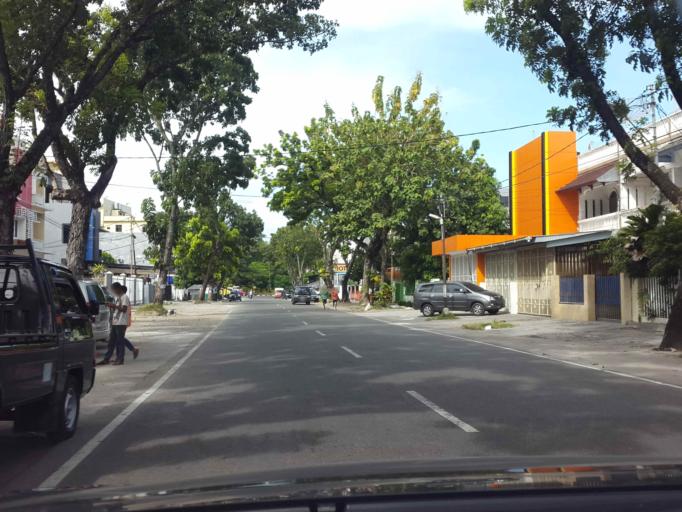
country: ID
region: West Sumatra
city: Padang
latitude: -0.9570
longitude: 100.3538
